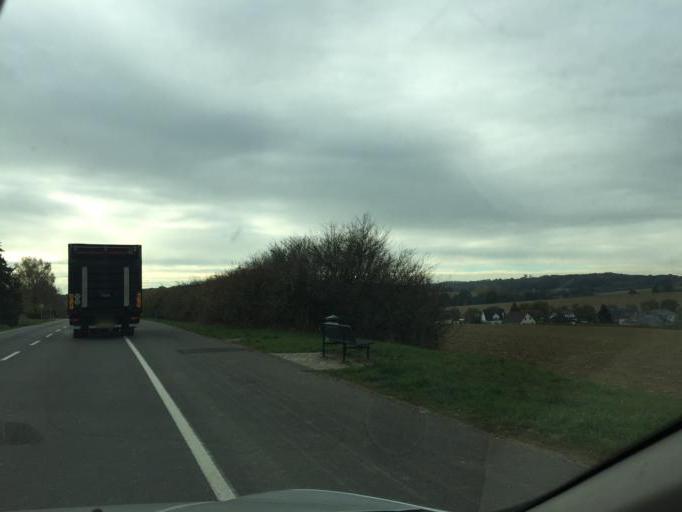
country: LU
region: Luxembourg
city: Capellen
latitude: 49.6198
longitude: 5.9831
